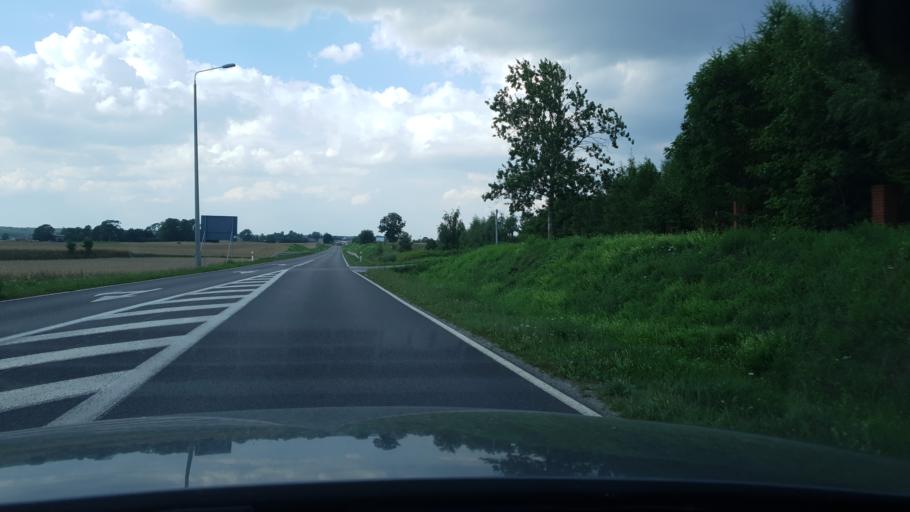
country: PL
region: Kujawsko-Pomorskie
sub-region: Powiat wabrzeski
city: Wabrzezno
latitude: 53.2873
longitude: 18.9277
